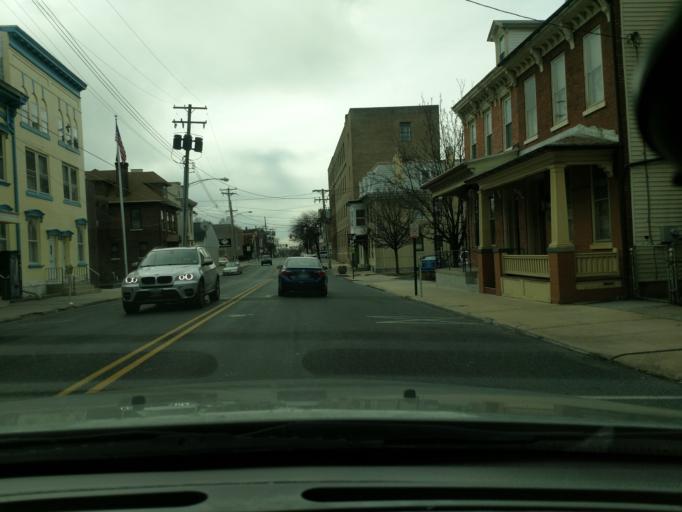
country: US
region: Pennsylvania
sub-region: Lebanon County
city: Lebanon
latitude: 40.3381
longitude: -76.4230
